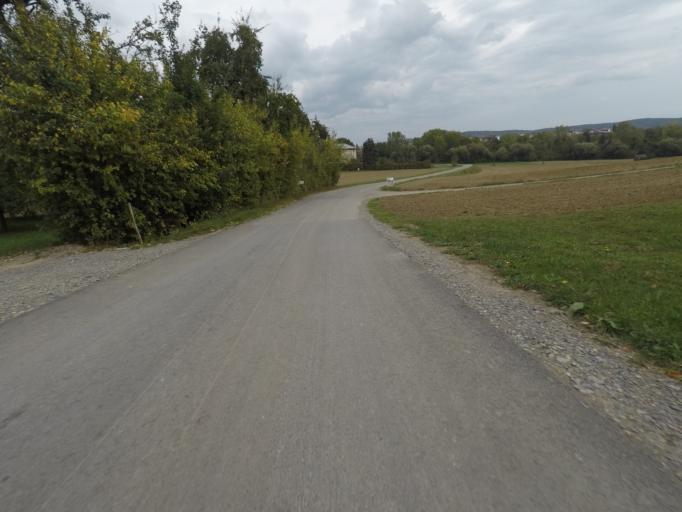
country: DE
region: Baden-Wuerttemberg
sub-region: Regierungsbezirk Stuttgart
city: Herrenberg
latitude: 48.5845
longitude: 8.8506
